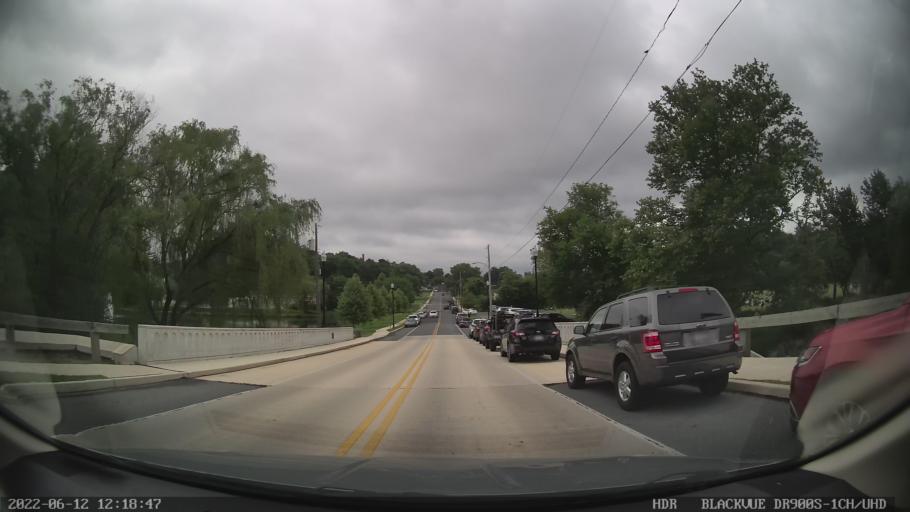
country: US
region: Pennsylvania
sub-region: Lehigh County
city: Allentown
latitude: 40.5921
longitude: -75.4980
